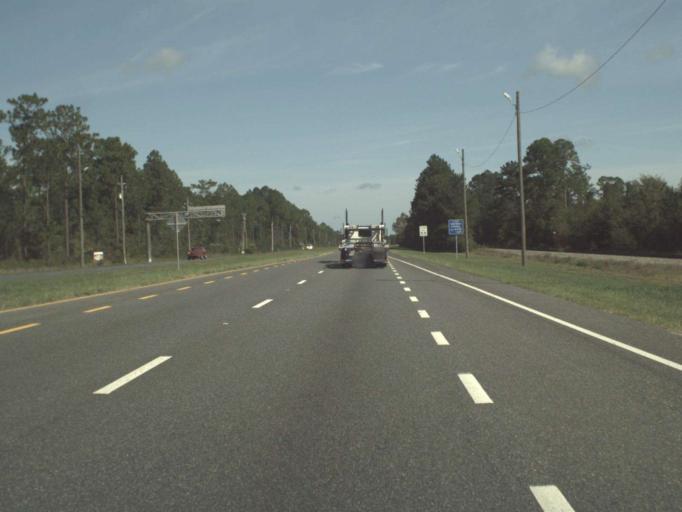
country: US
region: Florida
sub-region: Bay County
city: Youngstown
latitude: 30.4364
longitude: -85.4271
